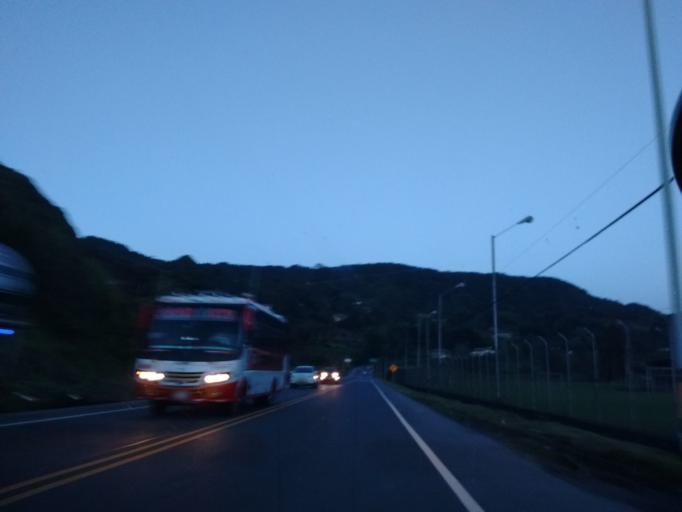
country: CO
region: Antioquia
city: Santuario
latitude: 6.1243
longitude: -75.2414
